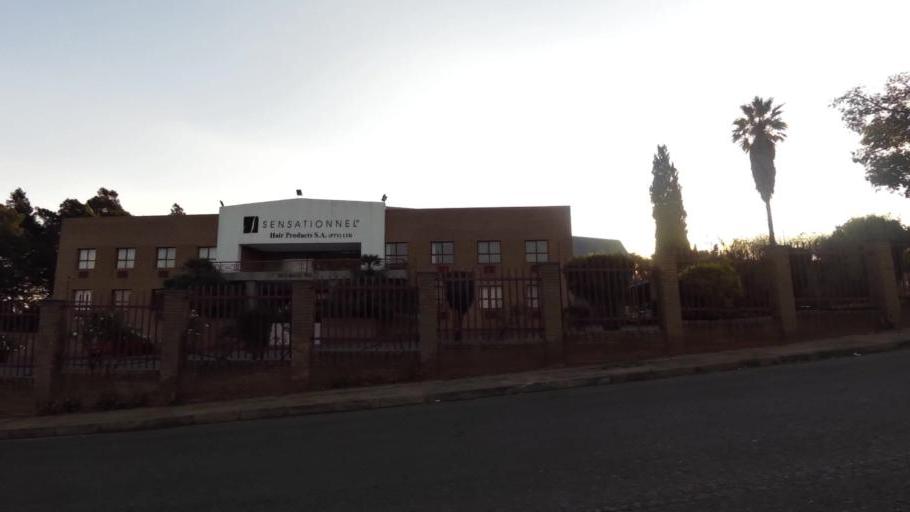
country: ZA
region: Gauteng
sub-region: City of Johannesburg Metropolitan Municipality
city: Roodepoort
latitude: -26.1798
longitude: 27.9444
